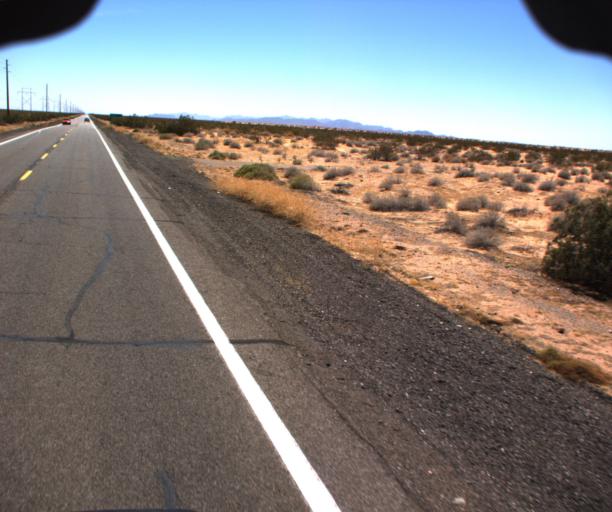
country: US
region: Arizona
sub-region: La Paz County
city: Parker
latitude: 33.9138
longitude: -114.2169
